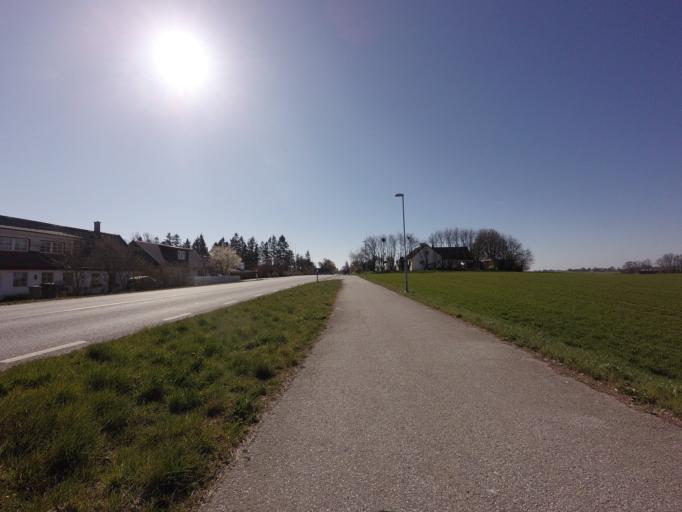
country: SE
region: Skane
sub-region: Malmo
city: Oxie
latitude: 55.4832
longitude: 13.1260
